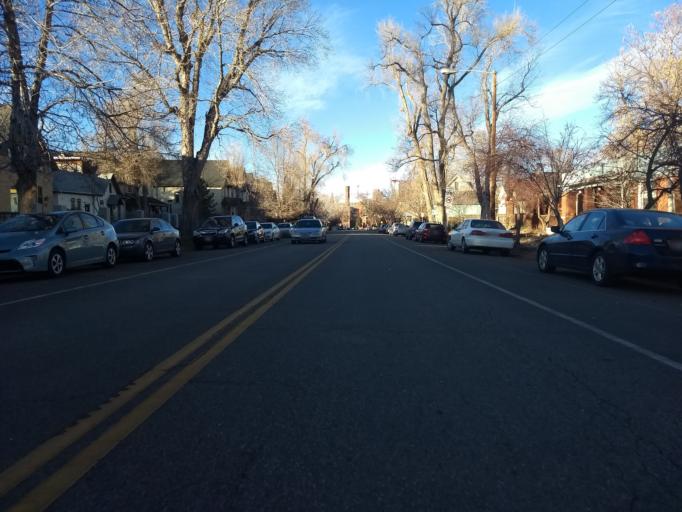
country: US
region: Colorado
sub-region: Denver County
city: Denver
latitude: 39.7214
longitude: -104.9908
